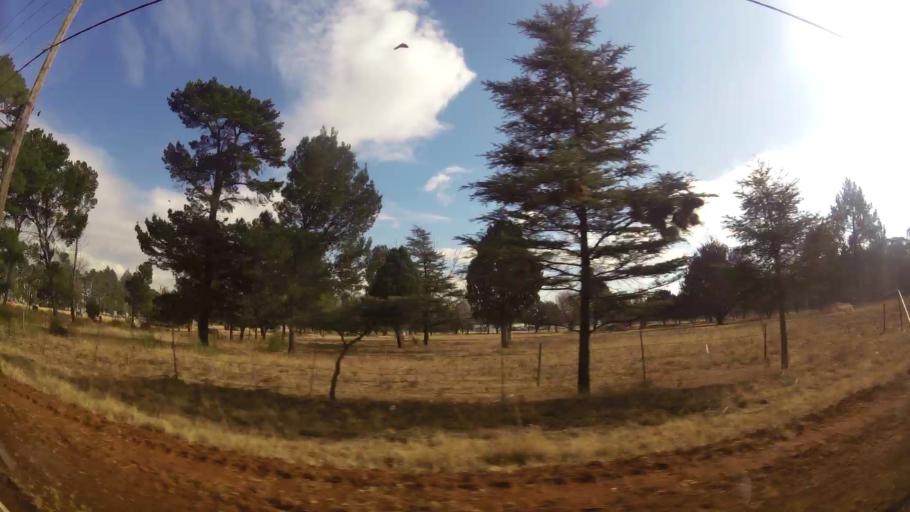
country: ZA
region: Gauteng
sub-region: Sedibeng District Municipality
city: Meyerton
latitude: -26.5526
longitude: 28.0549
